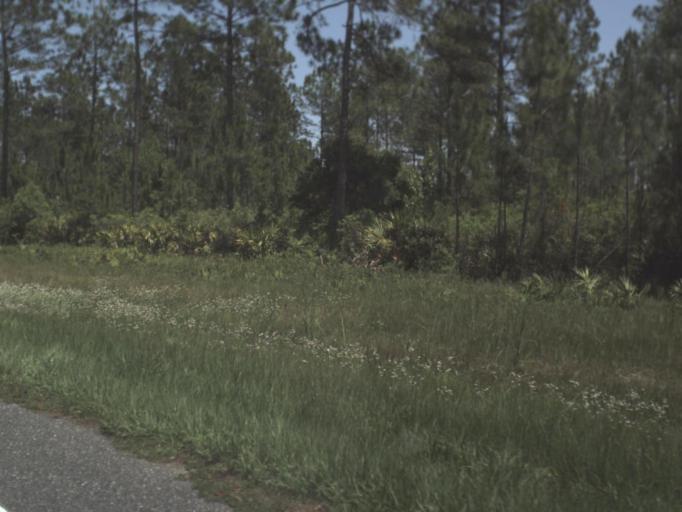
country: US
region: Florida
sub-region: Baker County
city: Macclenny
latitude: 30.2449
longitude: -82.2865
